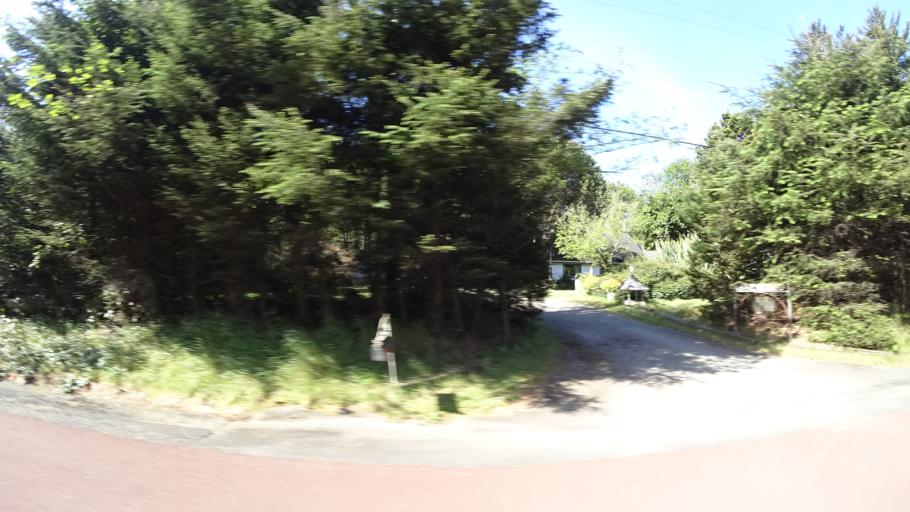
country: US
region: Oregon
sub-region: Curry County
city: Harbor
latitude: 41.9499
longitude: -124.2003
